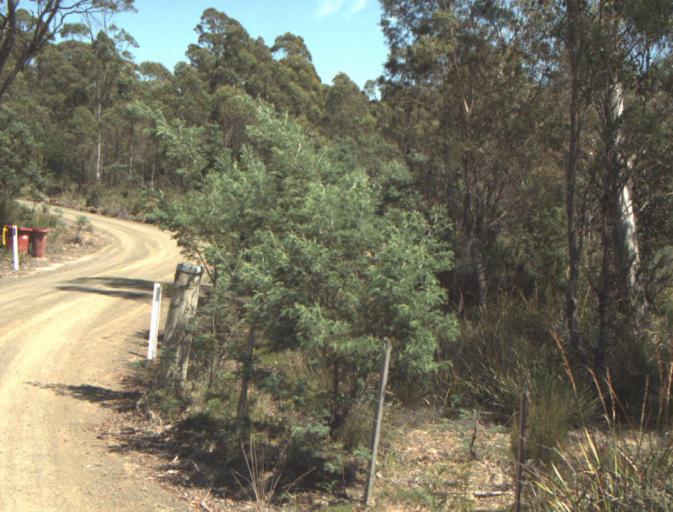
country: AU
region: Tasmania
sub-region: Launceston
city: Mayfield
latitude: -41.2796
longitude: 147.0958
